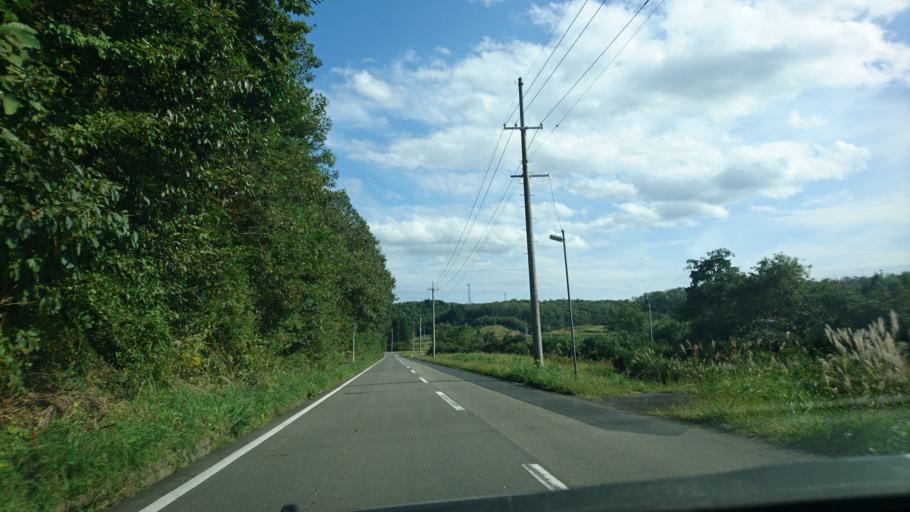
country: JP
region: Iwate
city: Ichinoseki
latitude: 38.8711
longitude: 141.0891
